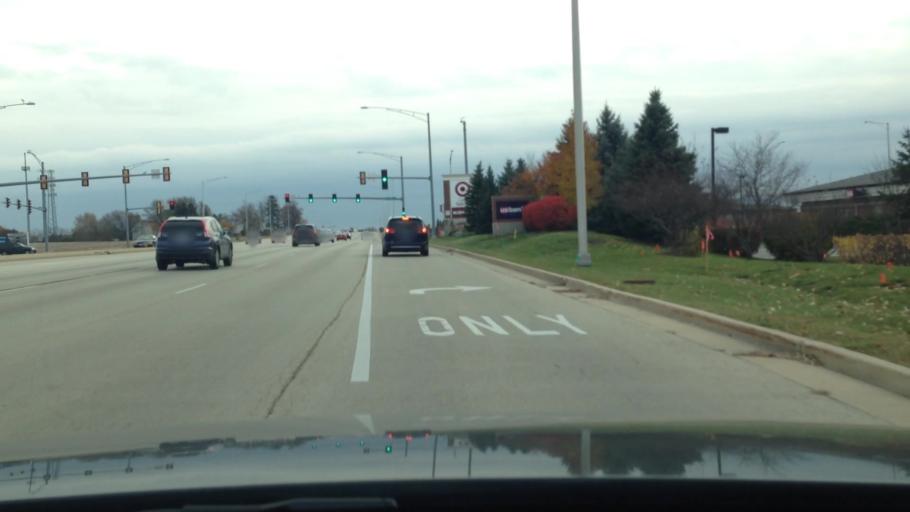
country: US
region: Illinois
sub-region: McHenry County
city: Lake in the Hills
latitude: 42.1623
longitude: -88.3358
